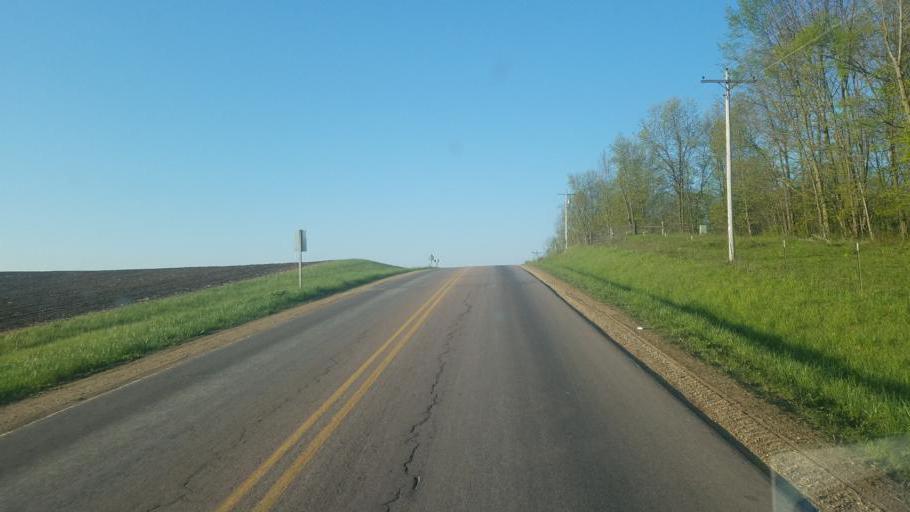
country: US
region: Wisconsin
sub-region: Vernon County
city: Hillsboro
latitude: 43.6443
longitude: -90.4525
